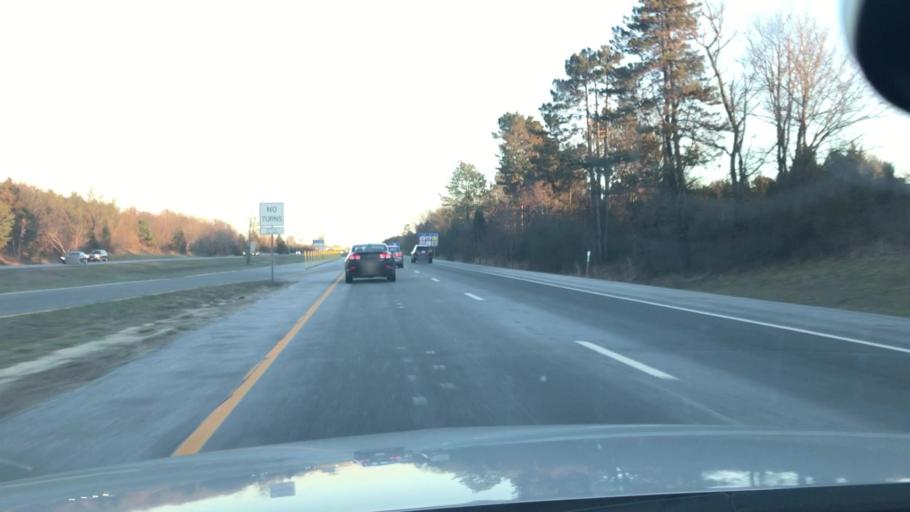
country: US
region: New Jersey
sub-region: Gloucester County
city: Turnersville
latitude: 39.7419
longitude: -75.0174
